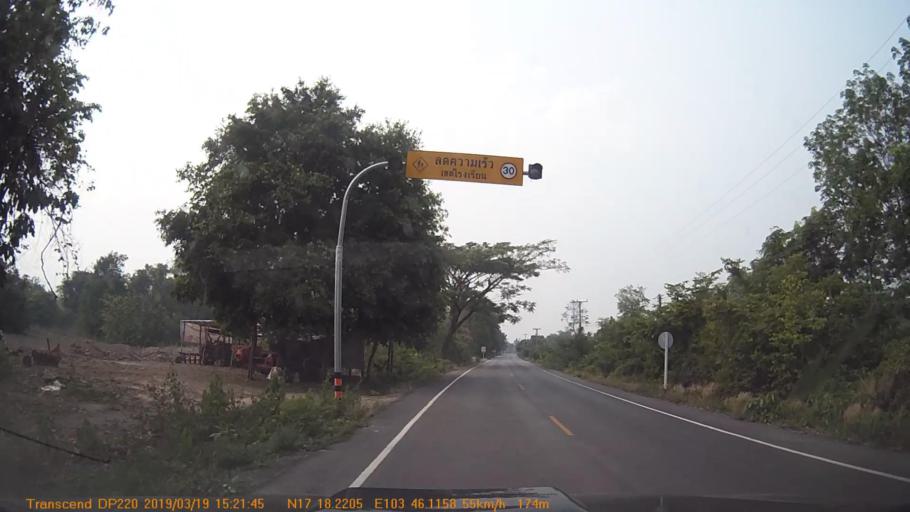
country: TH
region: Sakon Nakhon
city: Phanna Nikhom
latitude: 17.3038
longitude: 103.7685
